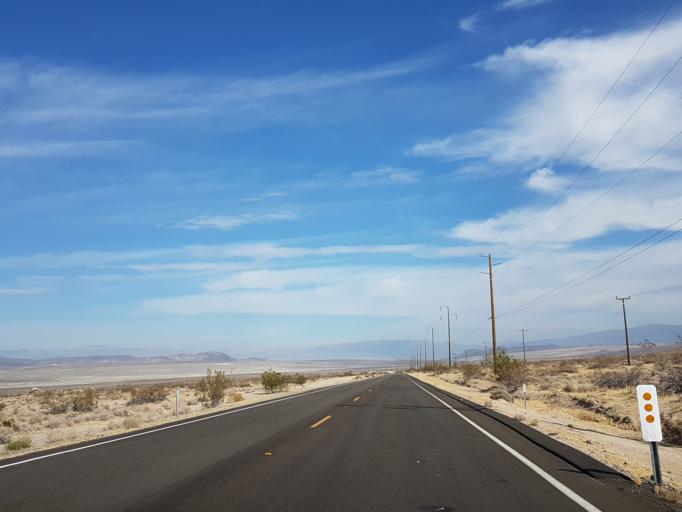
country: US
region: California
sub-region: Kern County
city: Ridgecrest
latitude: 35.6408
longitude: -117.5549
